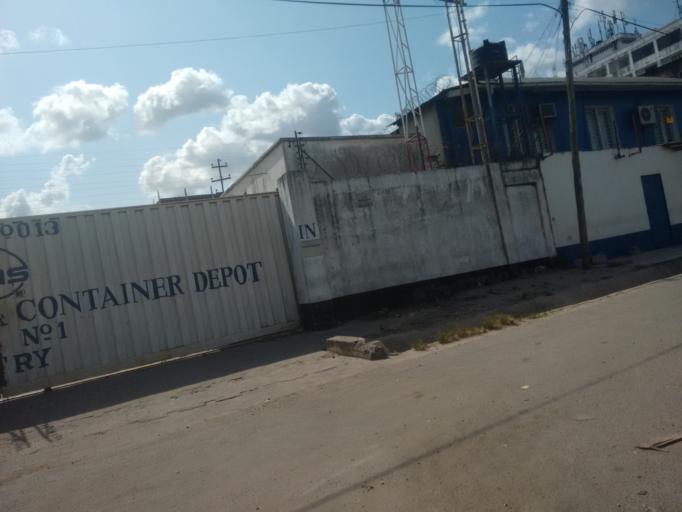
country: TZ
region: Dar es Salaam
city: Dar es Salaam
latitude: -6.8354
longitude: 39.2693
